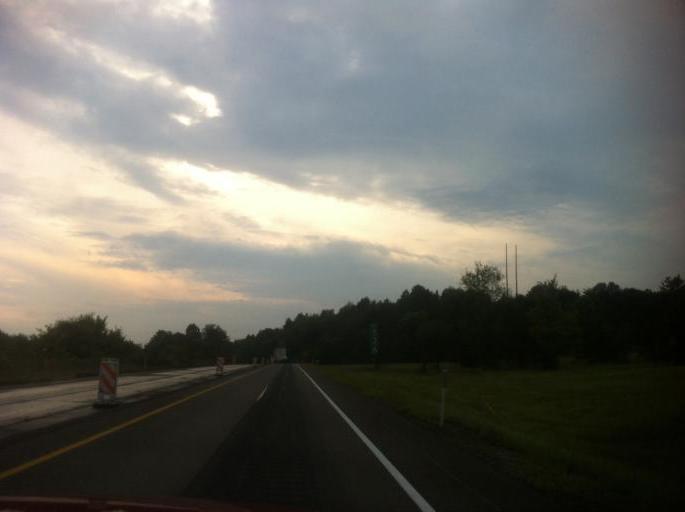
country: US
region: Pennsylvania
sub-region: Clarion County
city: Knox
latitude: 41.1849
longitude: -79.5423
